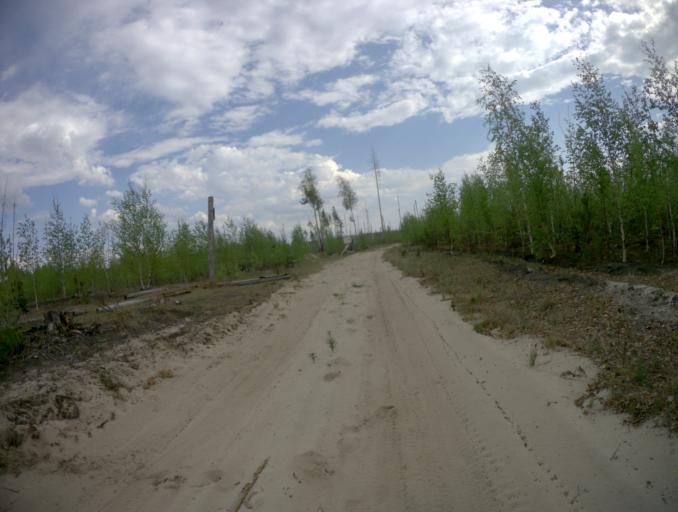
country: RU
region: Ivanovo
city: Talitsy
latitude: 56.4402
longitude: 42.2803
